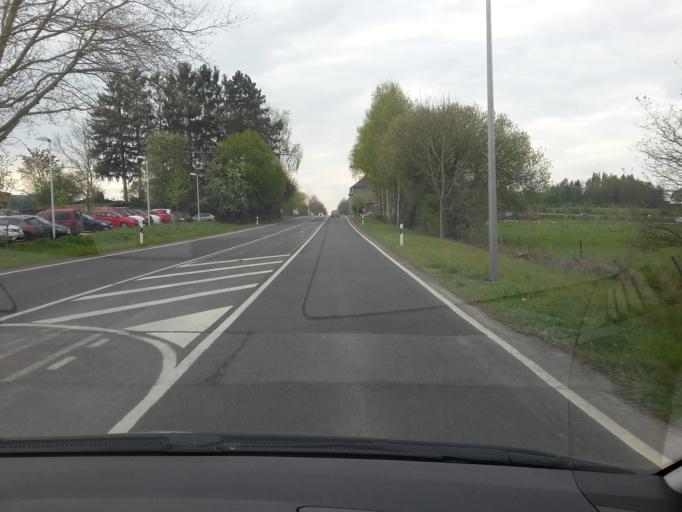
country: LU
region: Luxembourg
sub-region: Canton de Luxembourg
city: Bertrange
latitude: 49.5973
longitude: 6.0517
